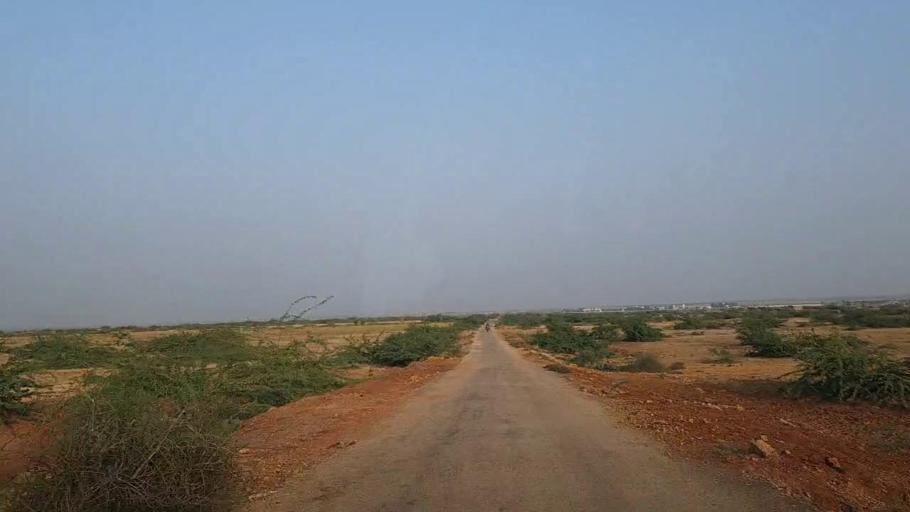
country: PK
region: Sindh
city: Thatta
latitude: 24.6905
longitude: 67.8296
